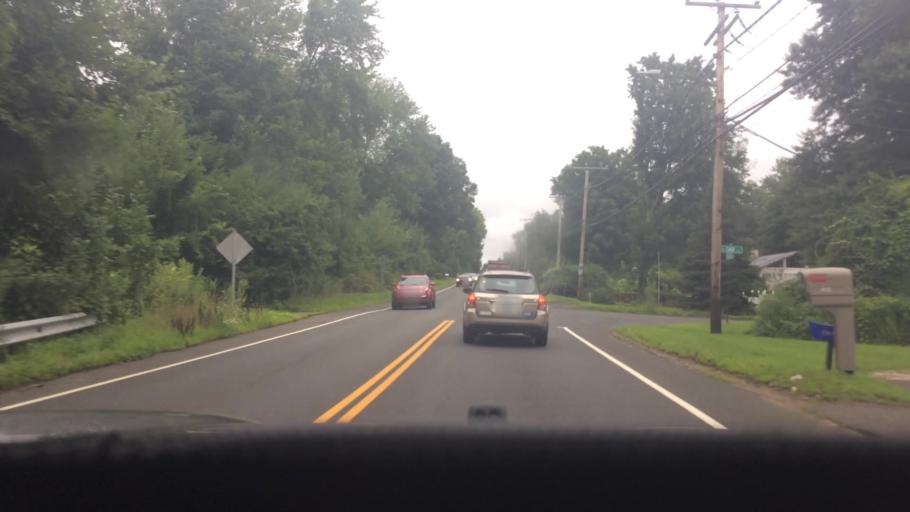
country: US
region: Connecticut
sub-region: Hartford County
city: Blue Hills
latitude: 41.8194
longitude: -72.7390
